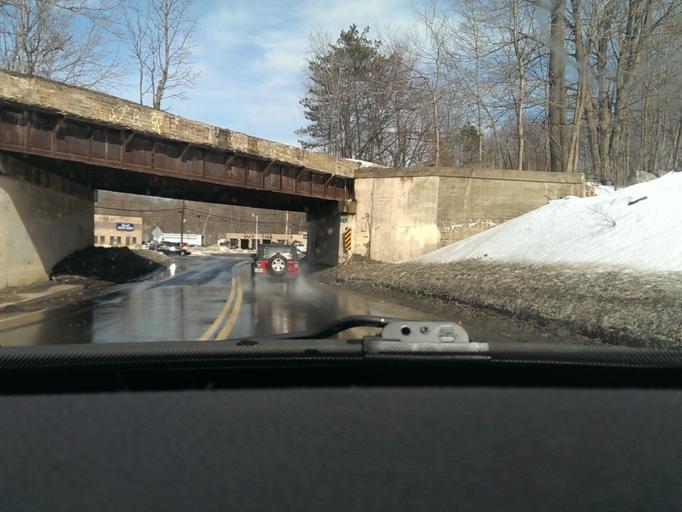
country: US
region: Massachusetts
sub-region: Hampden County
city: Wilbraham
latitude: 42.1540
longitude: -72.4210
